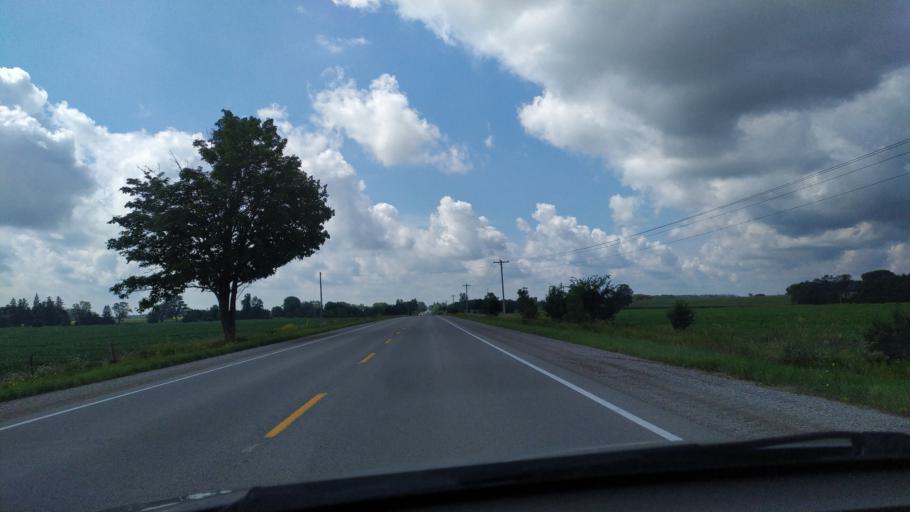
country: CA
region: Ontario
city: South Huron
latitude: 43.3450
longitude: -81.2961
